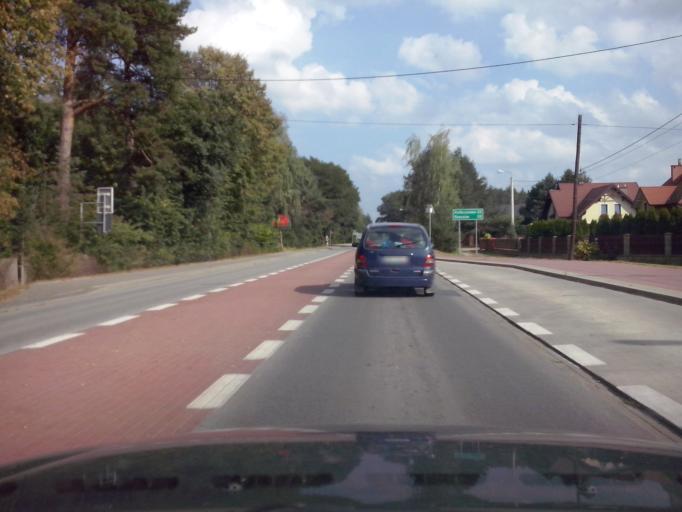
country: PL
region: Subcarpathian Voivodeship
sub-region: Powiat mielecki
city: Mielec
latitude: 50.2796
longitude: 21.4849
